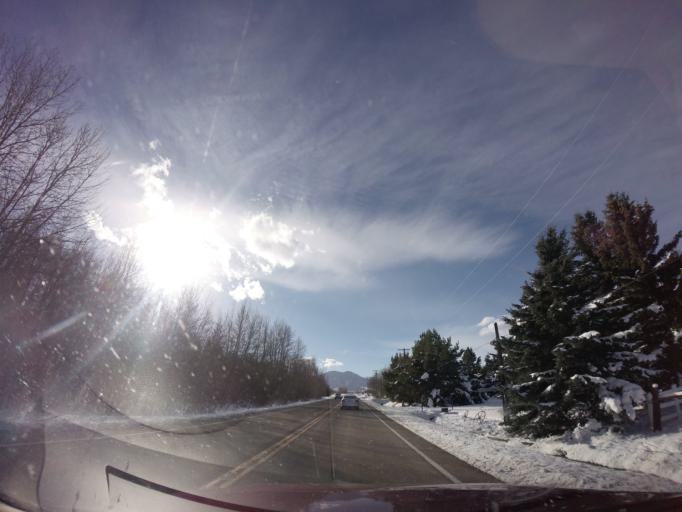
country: US
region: Montana
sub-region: Carbon County
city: Red Lodge
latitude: 45.2153
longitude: -109.2422
